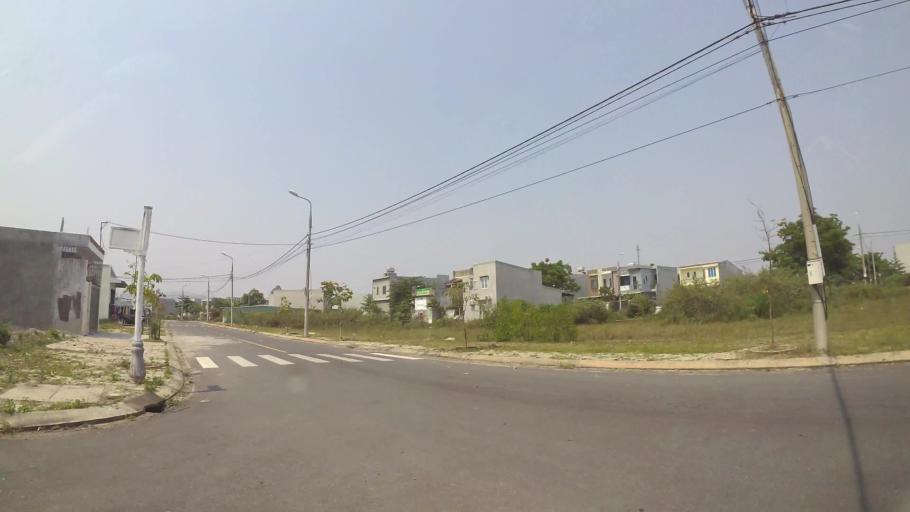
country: VN
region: Da Nang
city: Cam Le
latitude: 15.9907
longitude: 108.2040
